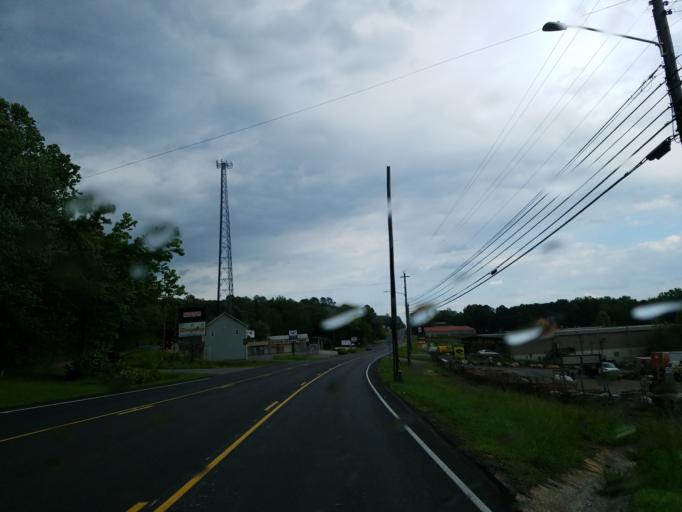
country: US
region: Georgia
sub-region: Pickens County
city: Jasper
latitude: 34.4645
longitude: -84.4180
